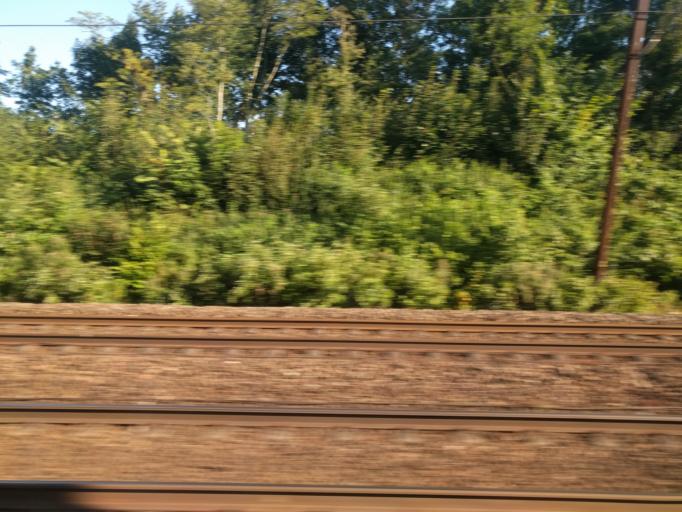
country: DK
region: Capital Region
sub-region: Hoje-Taastrup Kommune
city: Flong
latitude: 55.6447
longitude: 12.2320
